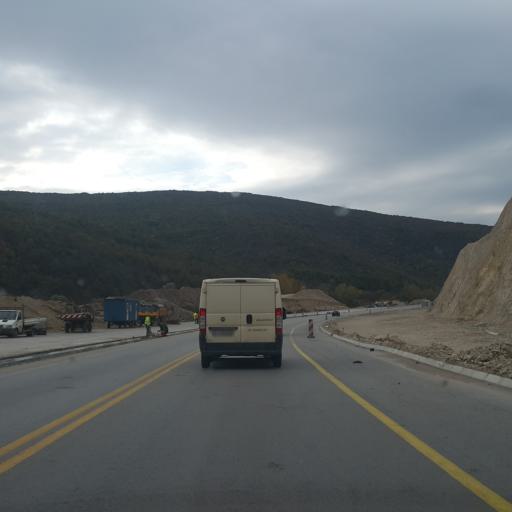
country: RS
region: Central Serbia
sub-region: Pirotski Okrug
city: Bela Palanka
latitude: 43.2252
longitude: 22.4297
